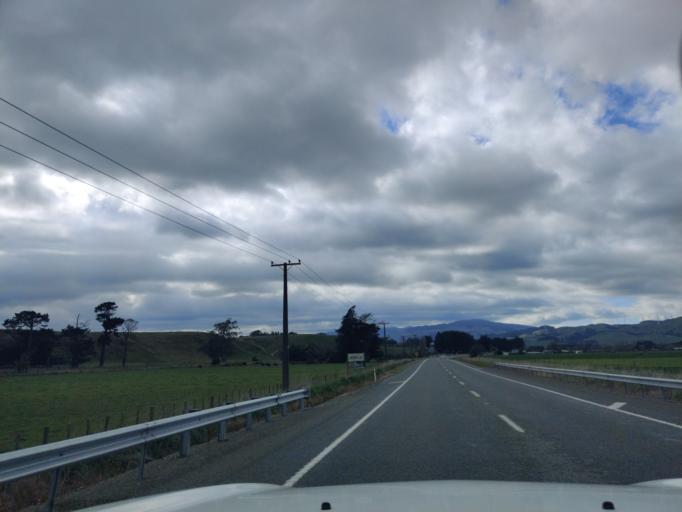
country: NZ
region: Manawatu-Wanganui
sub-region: Palmerston North City
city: Palmerston North
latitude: -40.3027
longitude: 175.7318
